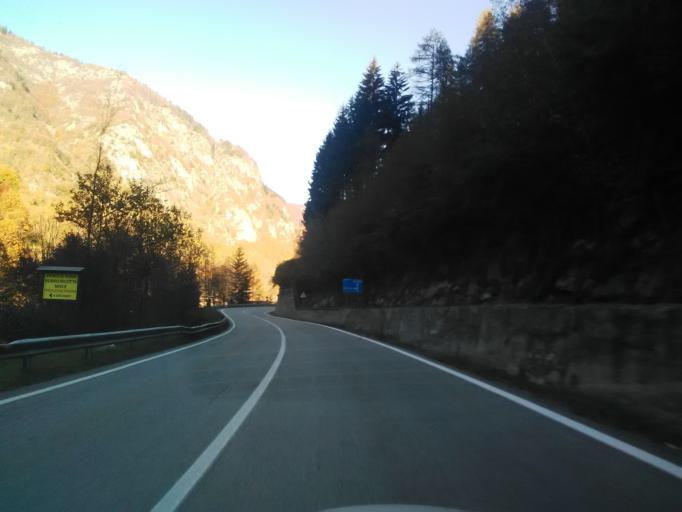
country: IT
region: Piedmont
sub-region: Provincia di Vercelli
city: Piode
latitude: 45.7800
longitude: 8.0456
